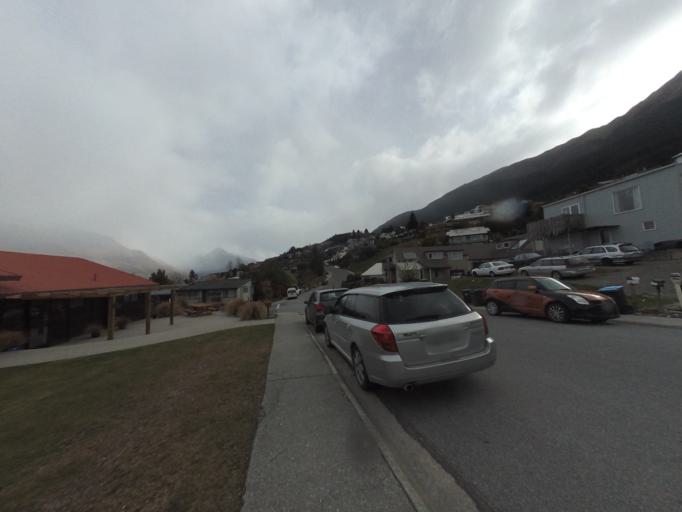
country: NZ
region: Otago
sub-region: Queenstown-Lakes District
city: Queenstown
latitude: -45.0390
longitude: 168.6380
